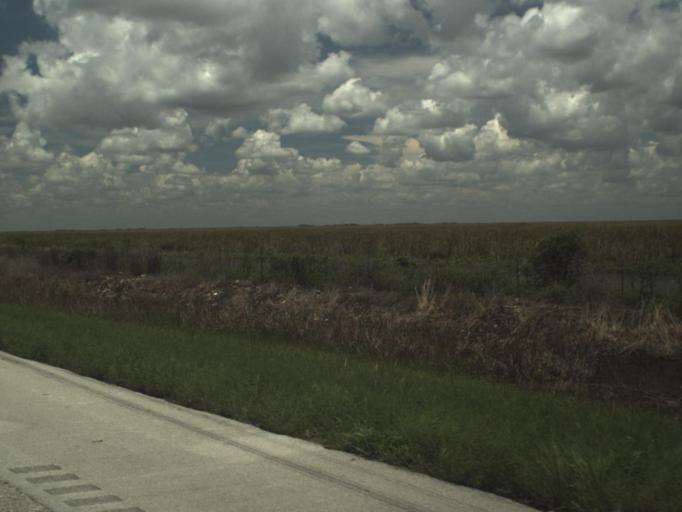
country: US
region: Florida
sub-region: Broward County
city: Weston
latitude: 26.1466
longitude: -80.6550
